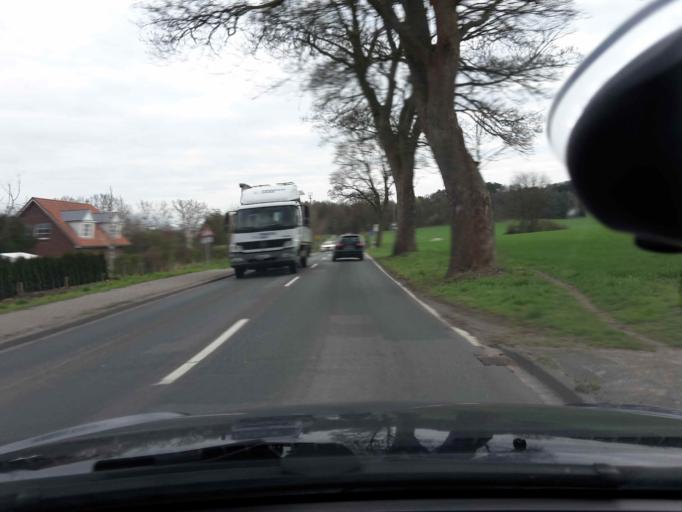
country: DE
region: Lower Saxony
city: Harmstorf
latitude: 53.3620
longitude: 9.9859
